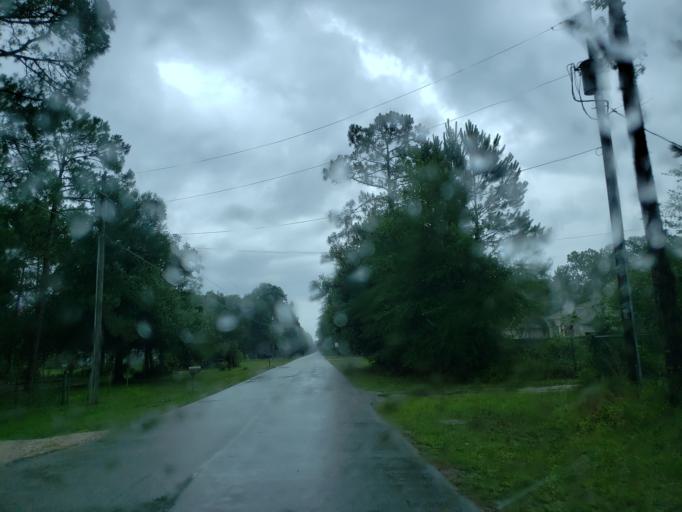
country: US
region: Florida
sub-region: Pasco County
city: Wesley Chapel
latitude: 28.2730
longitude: -82.3646
